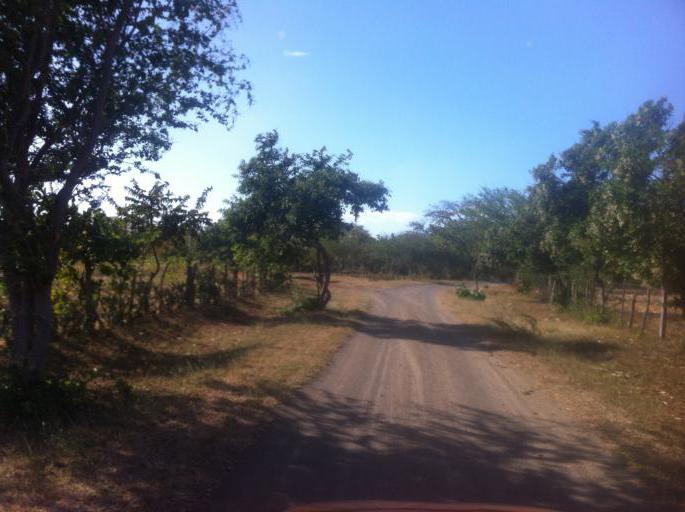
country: NI
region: Managua
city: Carlos Fonseca Amador
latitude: 11.9094
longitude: -86.6078
